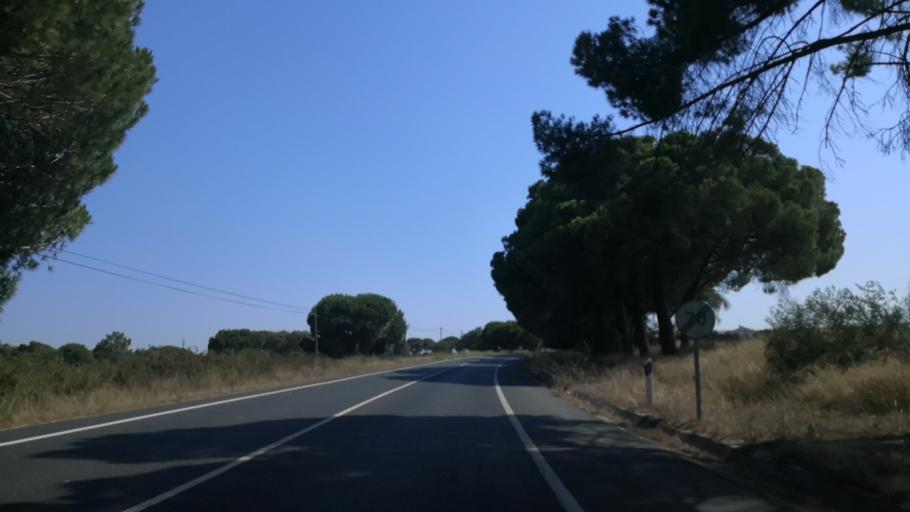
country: PT
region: Evora
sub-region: Vendas Novas
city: Vendas Novas
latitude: 38.7005
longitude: -8.6116
